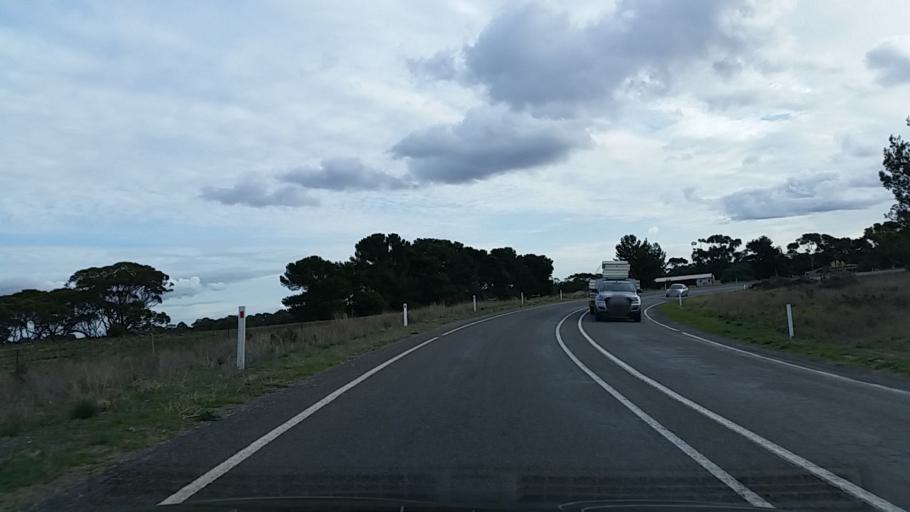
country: AU
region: South Australia
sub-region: Mount Barker
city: Callington
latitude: -35.1199
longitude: 139.1558
